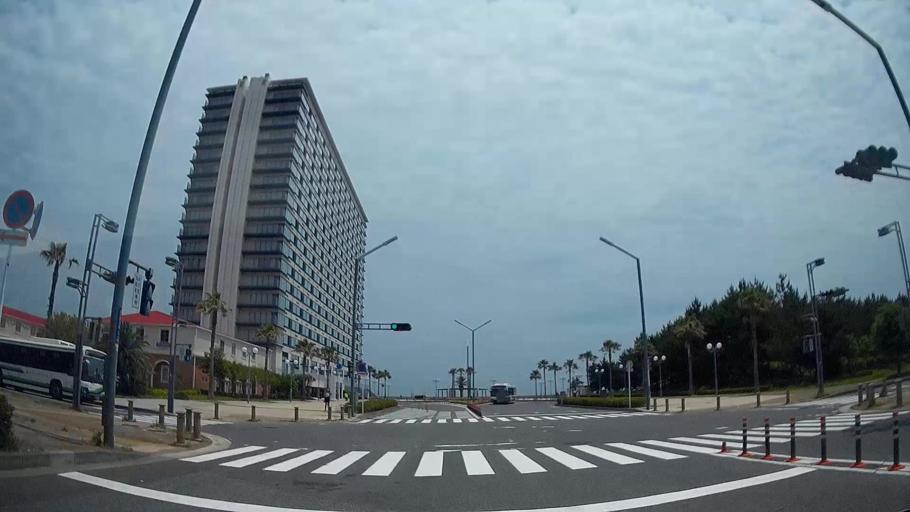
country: JP
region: Tokyo
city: Urayasu
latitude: 35.6378
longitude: 139.9305
